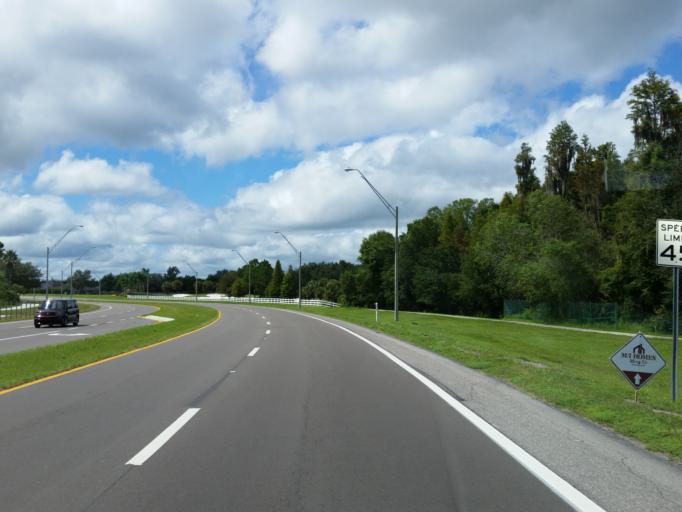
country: US
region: Florida
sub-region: Hillsborough County
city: Pebble Creek
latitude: 28.1471
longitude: -82.3083
